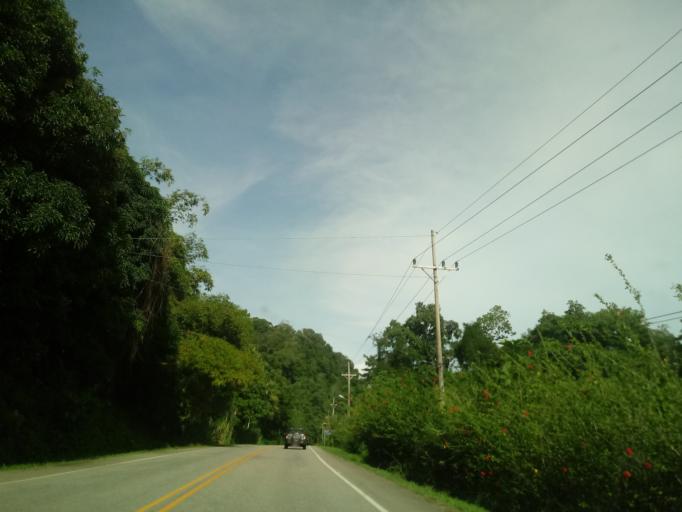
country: CR
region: San Jose
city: Daniel Flores
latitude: 9.2047
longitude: -83.7953
